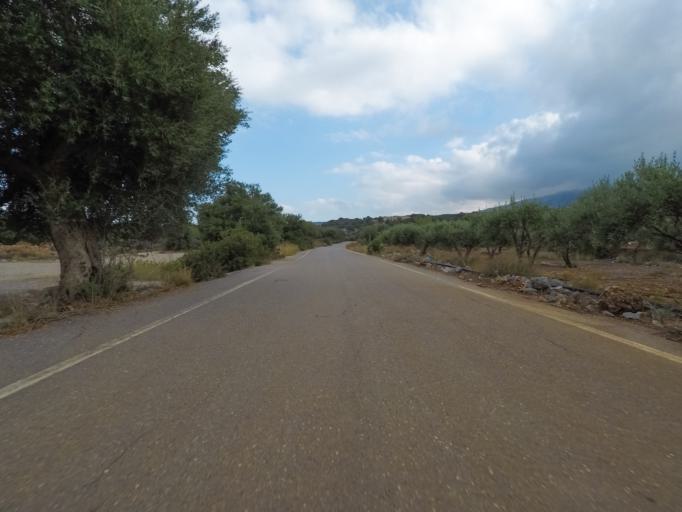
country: GR
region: Crete
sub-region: Nomos Lasithiou
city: Kritsa
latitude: 35.1730
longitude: 25.6535
